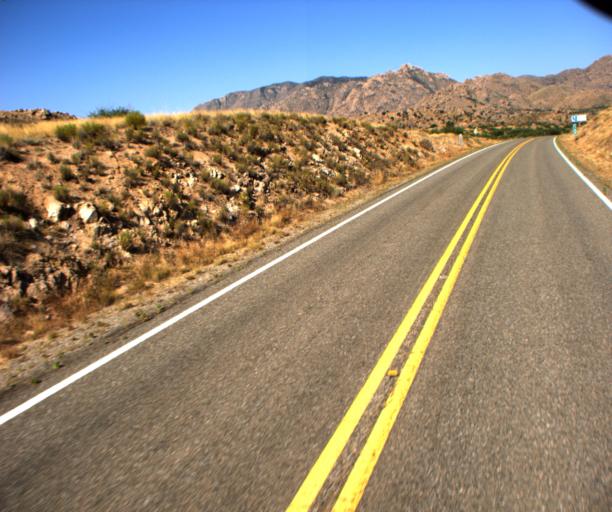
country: US
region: Arizona
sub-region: Graham County
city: Swift Trail Junction
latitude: 32.5605
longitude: -109.7432
